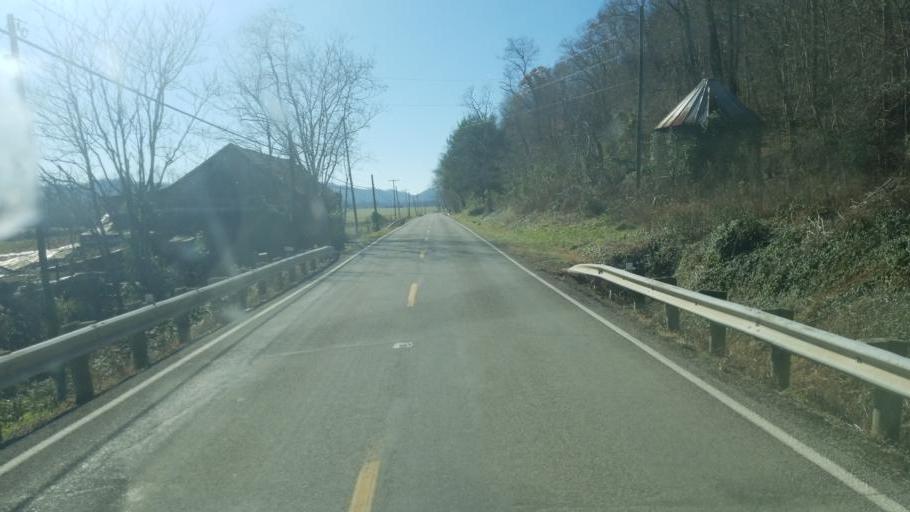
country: US
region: Ohio
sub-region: Scioto County
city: West Portsmouth
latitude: 38.6405
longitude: -83.1428
